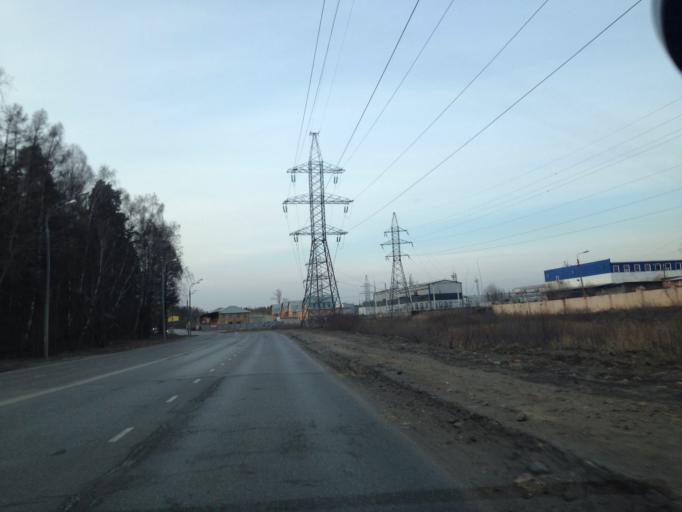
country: RU
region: Moscow
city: Vostochnyy
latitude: 55.7962
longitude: 37.8964
